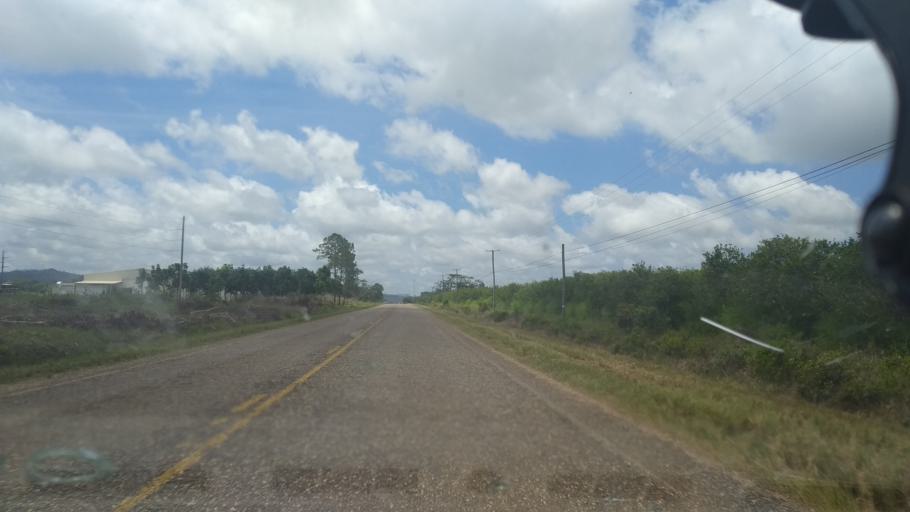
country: BZ
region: Stann Creek
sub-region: Dangriga
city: Dangriga
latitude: 16.7888
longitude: -88.3807
